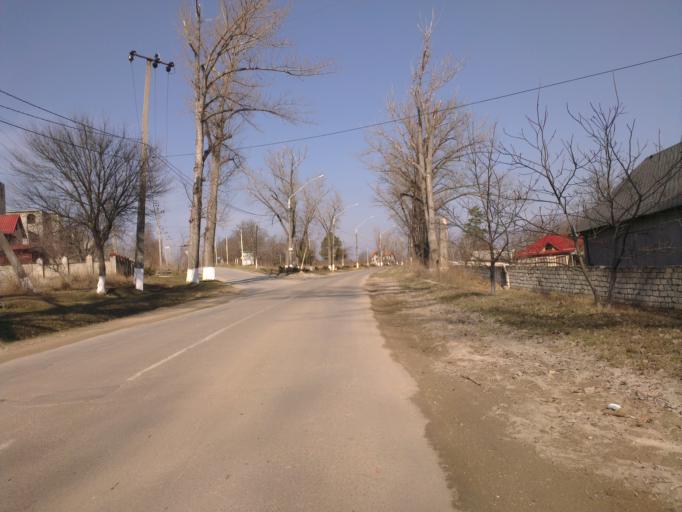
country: MD
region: Chisinau
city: Cricova
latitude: 47.1267
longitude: 28.8648
